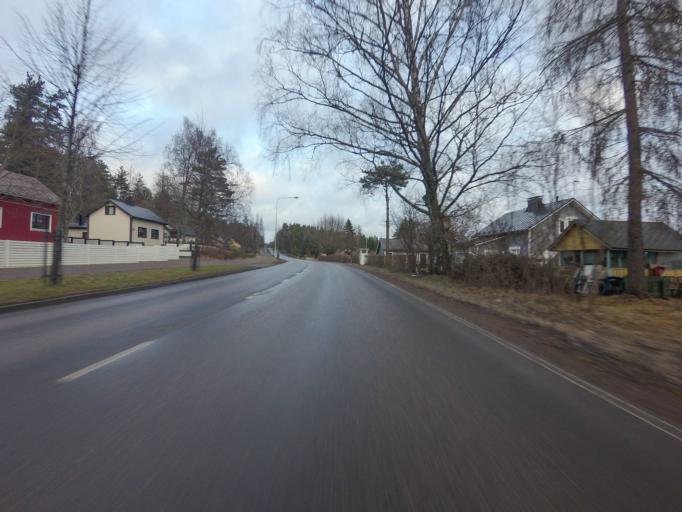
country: FI
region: Uusimaa
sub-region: Helsinki
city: Lohja
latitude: 60.2685
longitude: 24.1243
